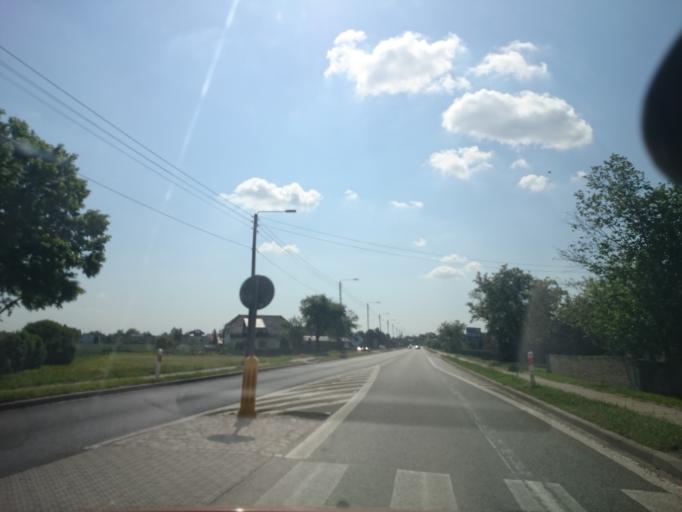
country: PL
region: Opole Voivodeship
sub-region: Powiat opolski
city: Naklo
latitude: 50.5841
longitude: 18.1081
